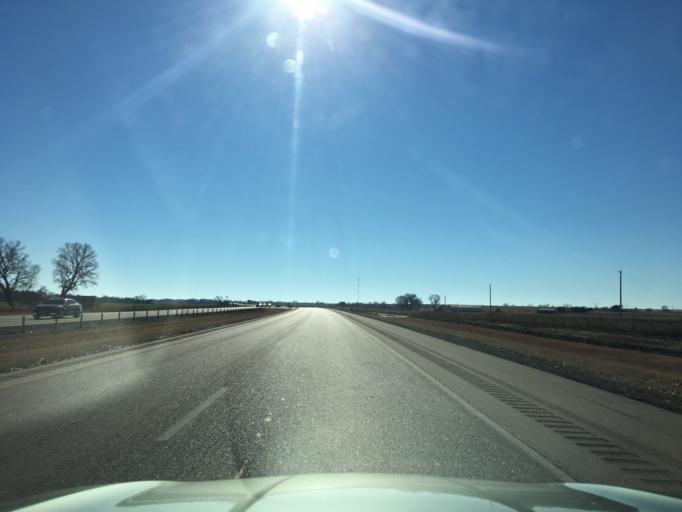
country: US
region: Oklahoma
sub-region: Kay County
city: Blackwell
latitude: 36.9001
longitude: -97.3543
